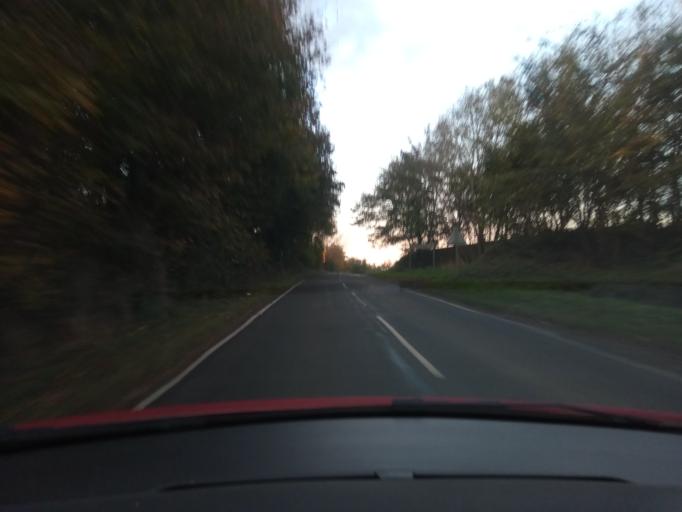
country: GB
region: England
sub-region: Northumberland
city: Bardon Mill
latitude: 54.9706
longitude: -2.2379
